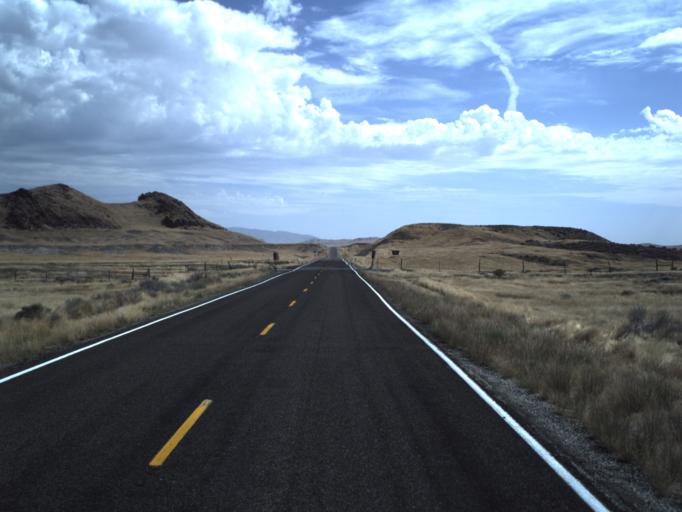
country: US
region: Nevada
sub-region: Elko County
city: West Wendover
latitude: 41.3730
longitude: -114.0225
